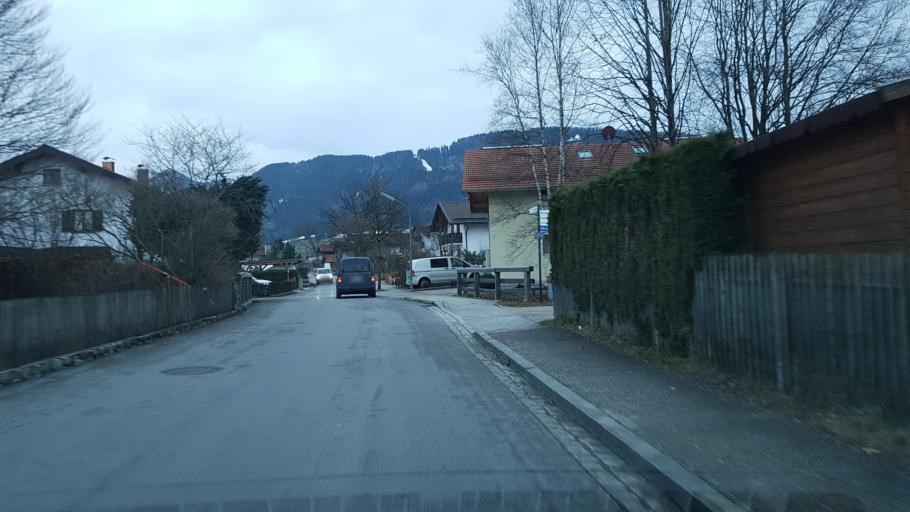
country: DE
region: Bavaria
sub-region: Upper Bavaria
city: Bernau am Chiemsee
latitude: 47.8117
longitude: 12.3788
